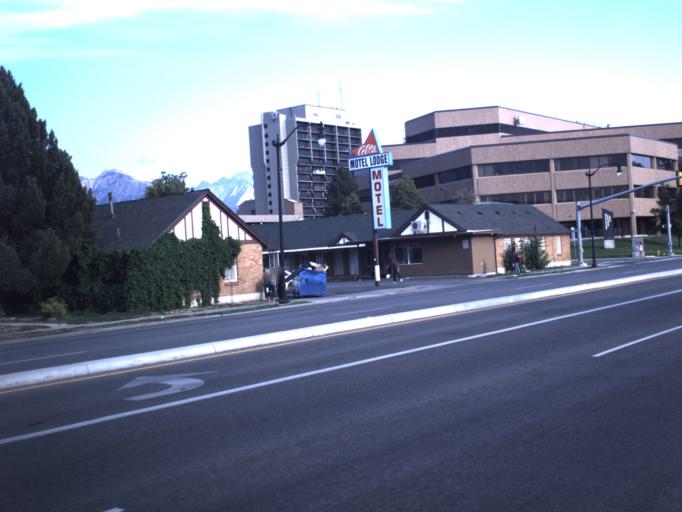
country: US
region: Utah
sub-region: Salt Lake County
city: South Salt Lake
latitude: 40.7295
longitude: -111.8884
